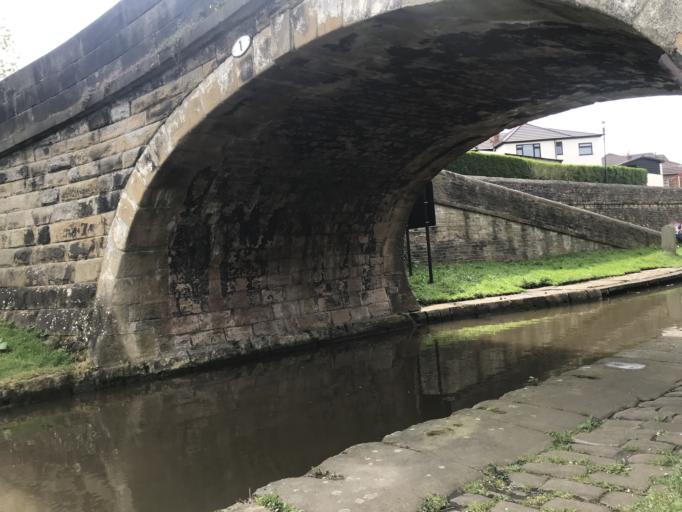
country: GB
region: England
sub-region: Borough of Stockport
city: Marple
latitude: 53.3926
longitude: -2.0594
